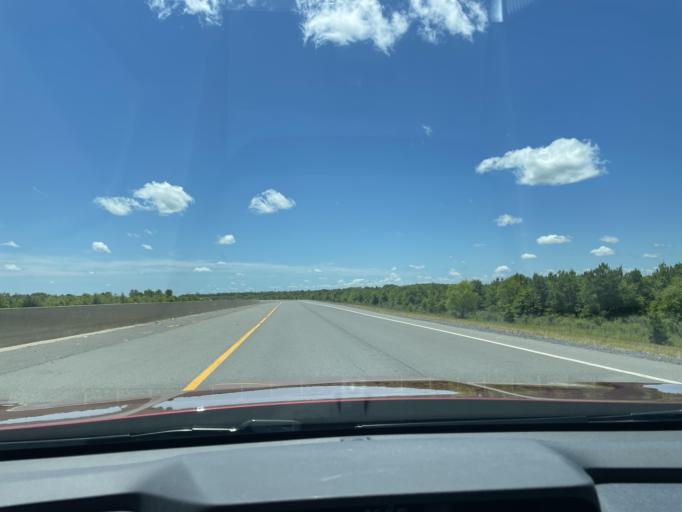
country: US
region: Arkansas
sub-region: Jefferson County
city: Pine Bluff
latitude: 34.1666
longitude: -91.9856
